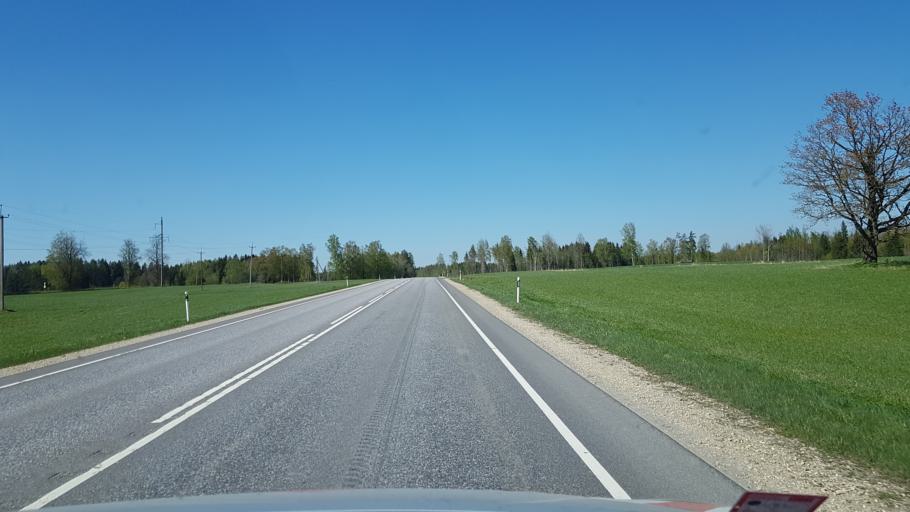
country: EE
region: Vorumaa
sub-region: Antsla vald
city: Vana-Antsla
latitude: 57.9929
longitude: 26.7651
